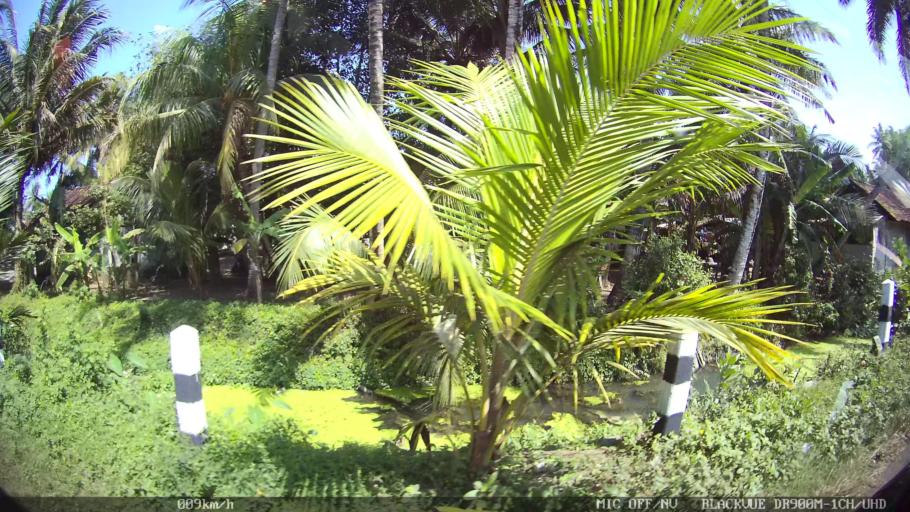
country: ID
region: Daerah Istimewa Yogyakarta
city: Srandakan
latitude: -7.9236
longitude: 110.1573
